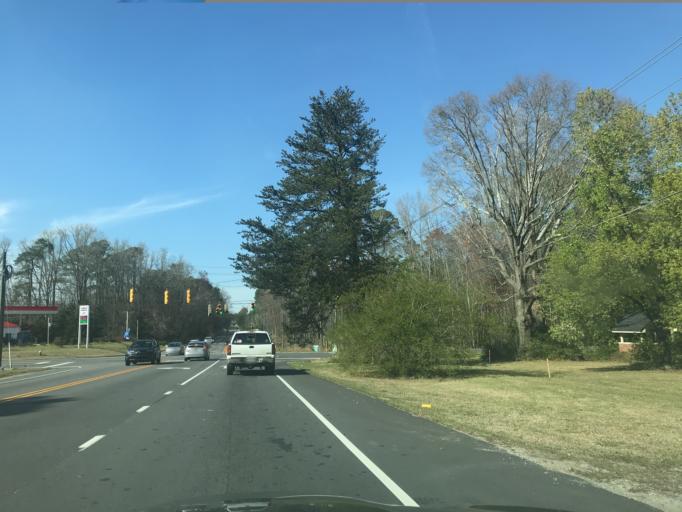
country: US
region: North Carolina
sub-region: Wake County
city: Fuquay-Varina
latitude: 35.5824
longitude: -78.7568
